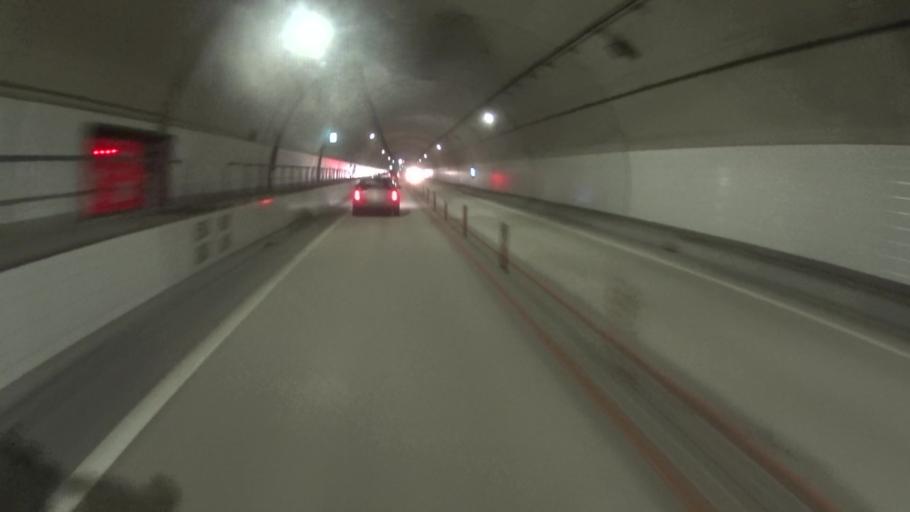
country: JP
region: Kyoto
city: Miyazu
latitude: 35.5383
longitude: 135.1597
